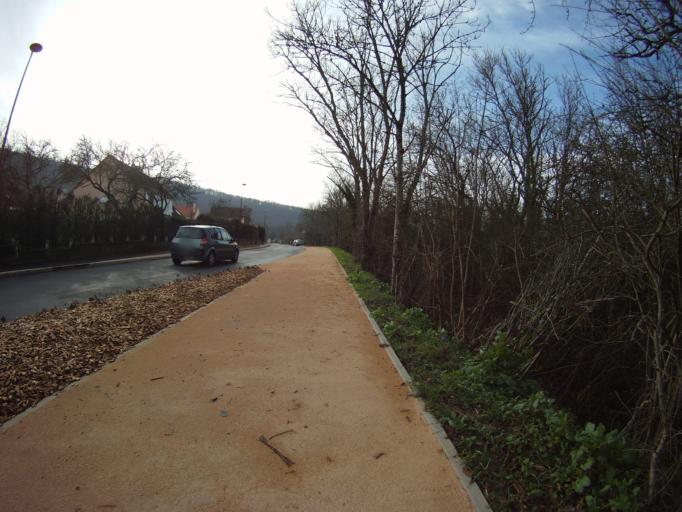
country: FR
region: Lorraine
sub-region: Departement de Meurthe-et-Moselle
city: Champigneulles
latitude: 48.7230
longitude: 6.1498
